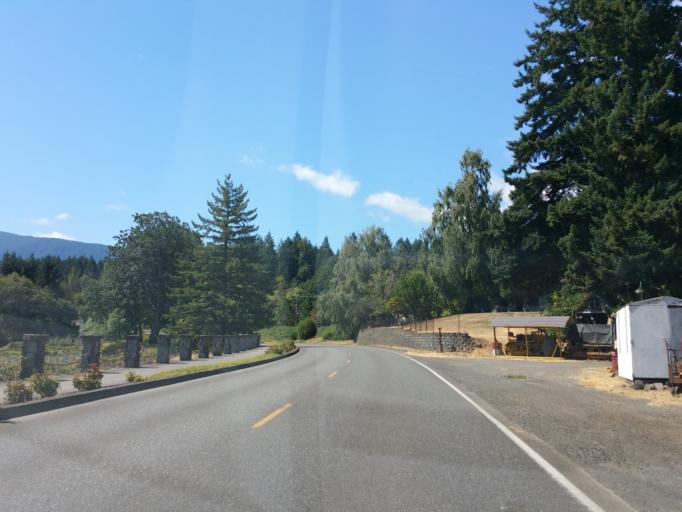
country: US
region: Washington
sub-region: Skamania County
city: Stevenson
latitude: 45.6915
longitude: -121.8981
